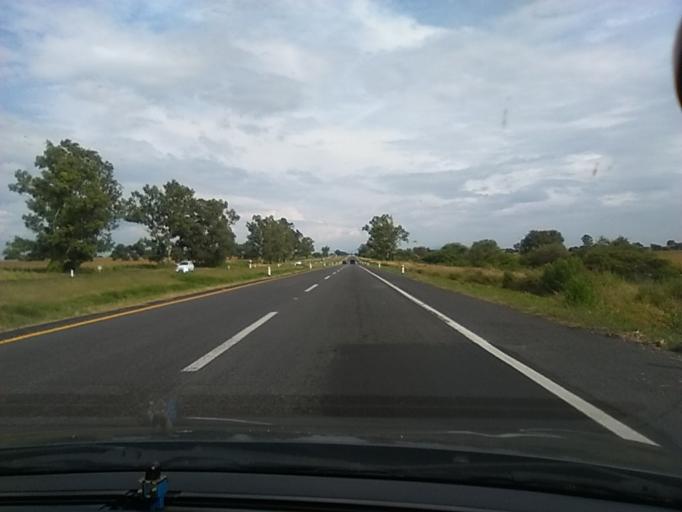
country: MX
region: Jalisco
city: La Barca
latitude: 20.3452
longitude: -102.6212
